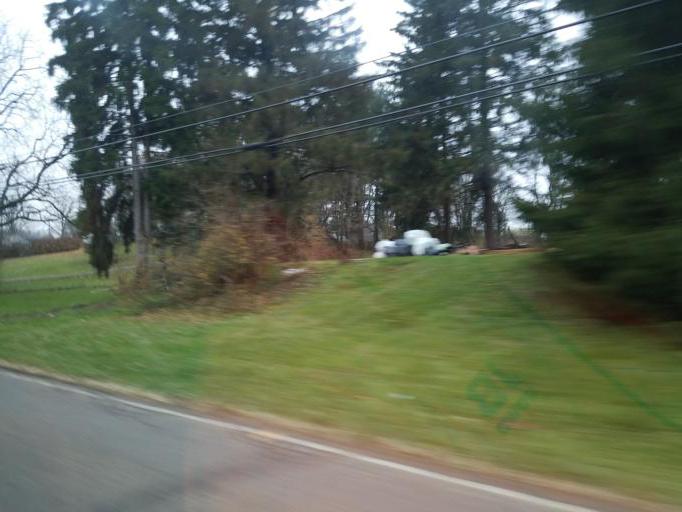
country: US
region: Ohio
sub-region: Richland County
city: Mansfield
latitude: 40.7061
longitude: -82.5115
